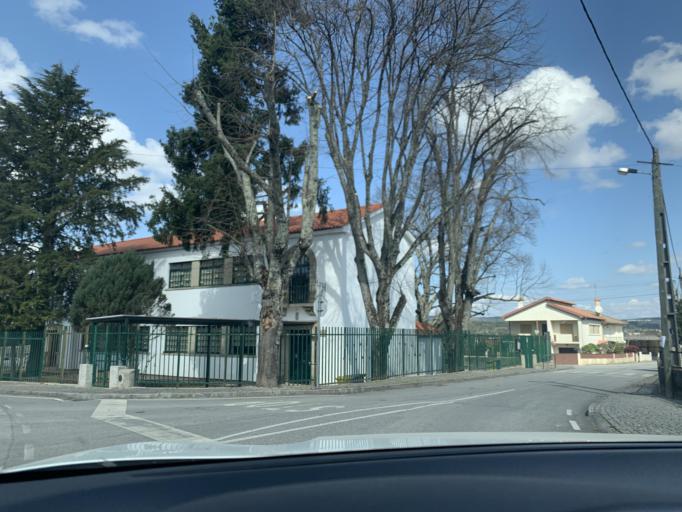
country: PT
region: Viseu
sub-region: Viseu
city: Rio de Loba
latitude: 40.6719
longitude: -7.8818
